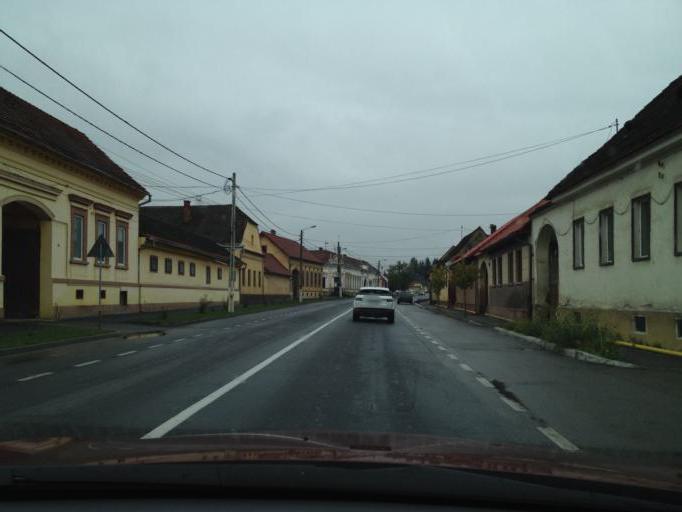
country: RO
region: Brasov
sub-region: Comuna Cristian
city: Cristian
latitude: 45.6210
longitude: 25.4789
